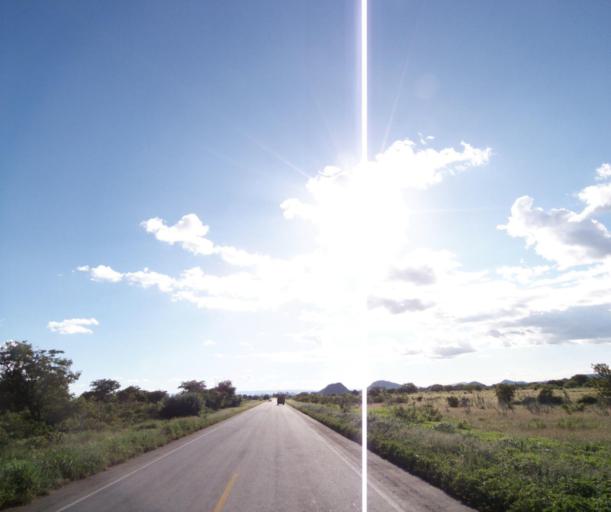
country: BR
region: Bahia
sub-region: Guanambi
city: Guanambi
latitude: -14.1598
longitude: -42.7122
